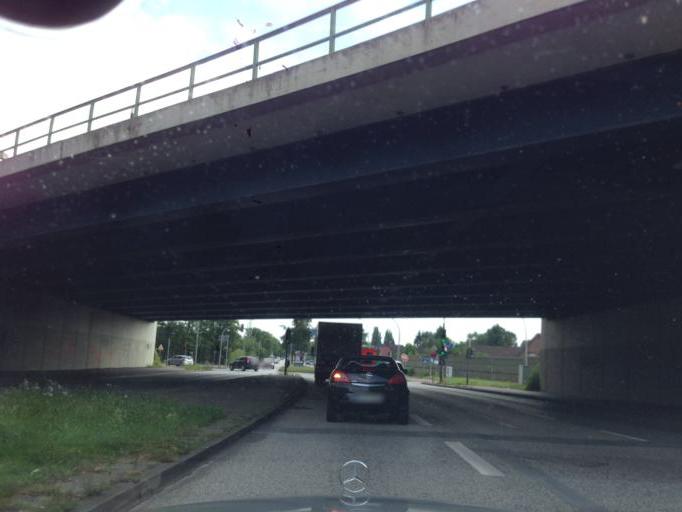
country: DE
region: Hamburg
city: Marienthal
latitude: 53.5455
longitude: 10.0832
